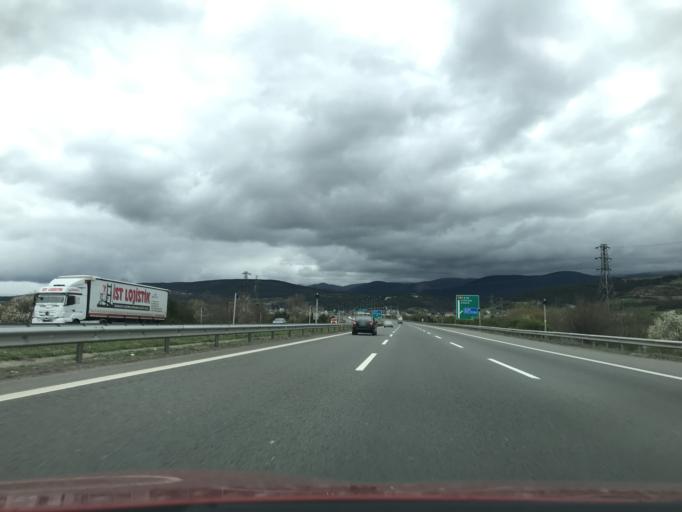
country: TR
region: Bolu
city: Bolu
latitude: 40.7646
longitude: 31.7546
